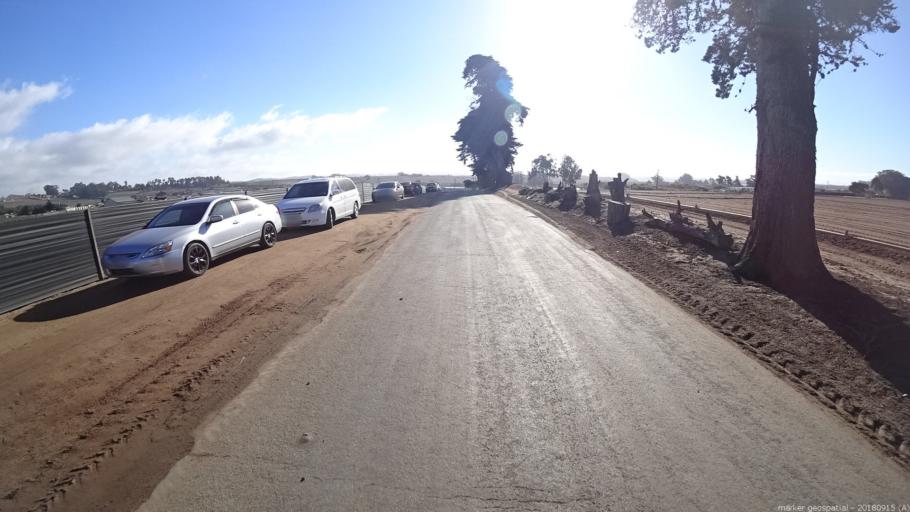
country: US
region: California
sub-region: Monterey County
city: Elkhorn
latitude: 36.8271
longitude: -121.7826
